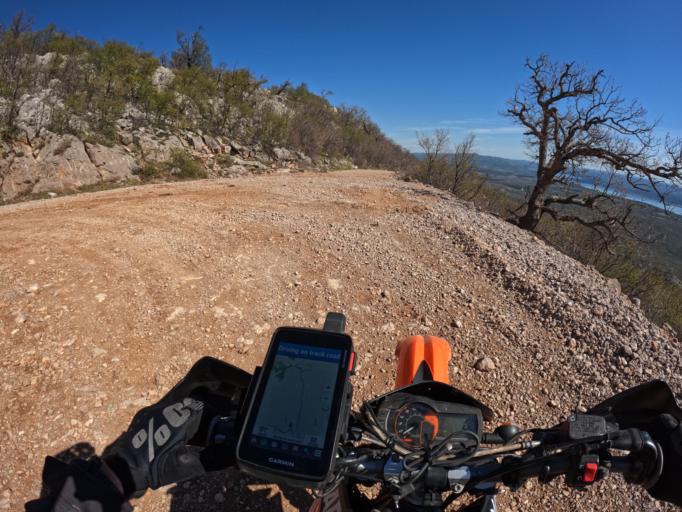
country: HR
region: Zadarska
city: Posedarje
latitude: 44.2798
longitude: 15.5594
